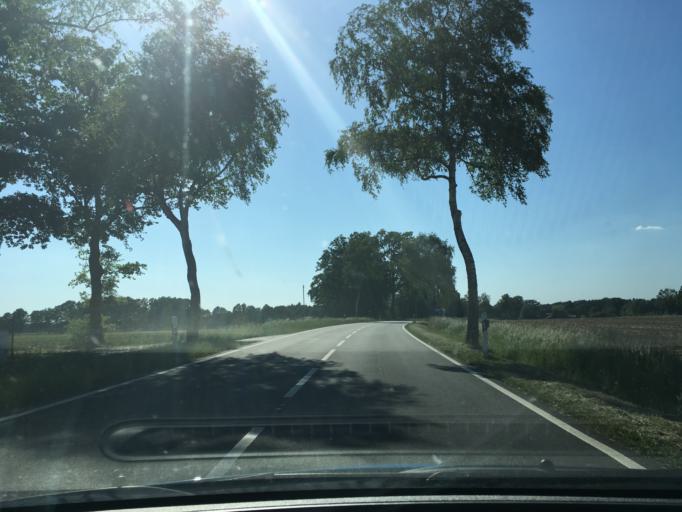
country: DE
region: Lower Saxony
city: Bad Fallingbostel
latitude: 52.9062
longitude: 9.7419
